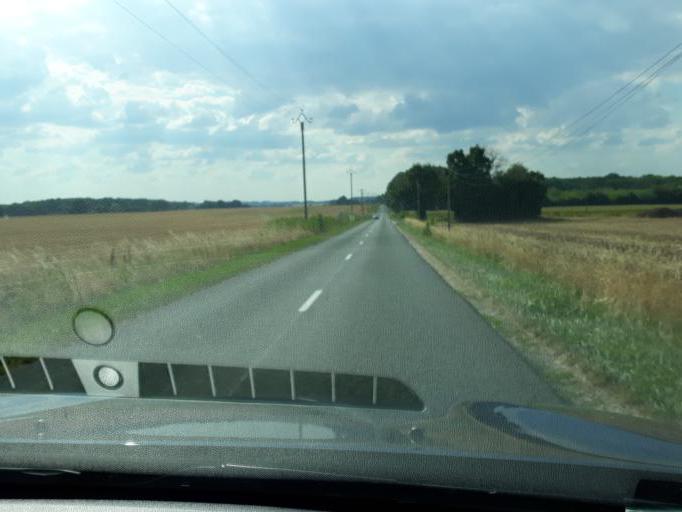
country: FR
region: Centre
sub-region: Departement du Cher
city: Nerondes
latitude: 47.0490
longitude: 2.8639
